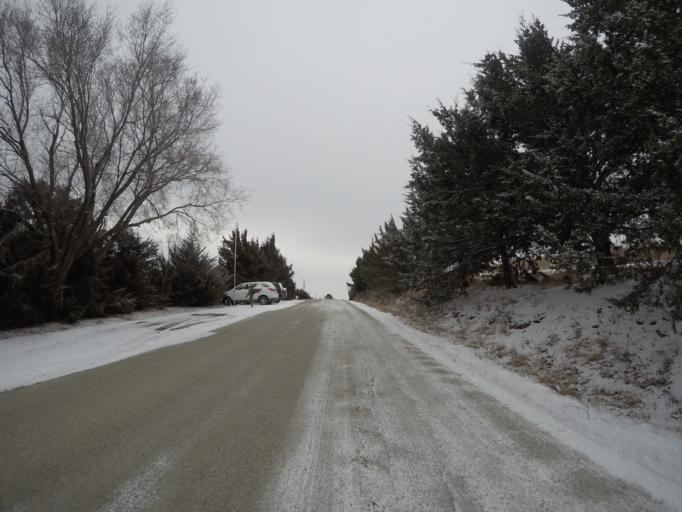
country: US
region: Kansas
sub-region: Wabaunsee County
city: Alma
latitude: 38.8612
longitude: -96.1868
